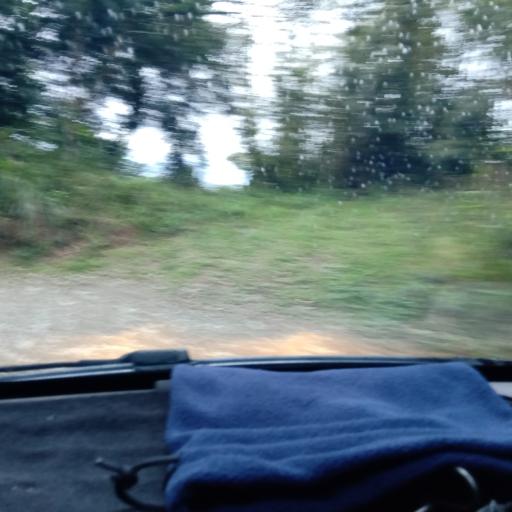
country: TW
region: Taiwan
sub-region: Yilan
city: Yilan
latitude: 24.8081
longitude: 121.6950
